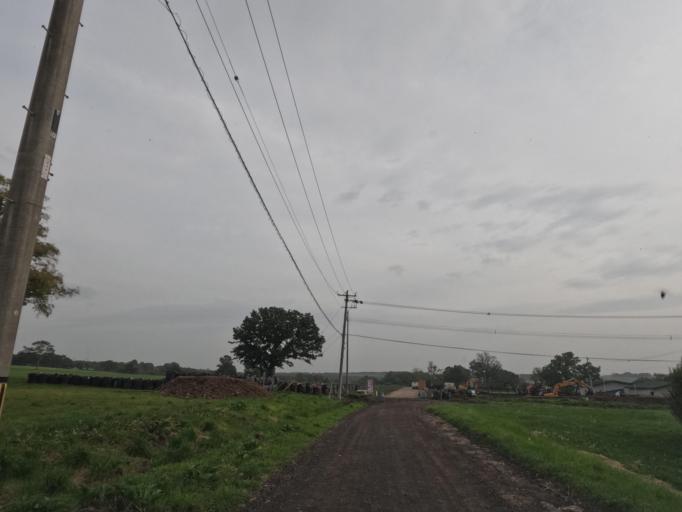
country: JP
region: Hokkaido
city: Date
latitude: 42.4249
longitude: 140.9166
